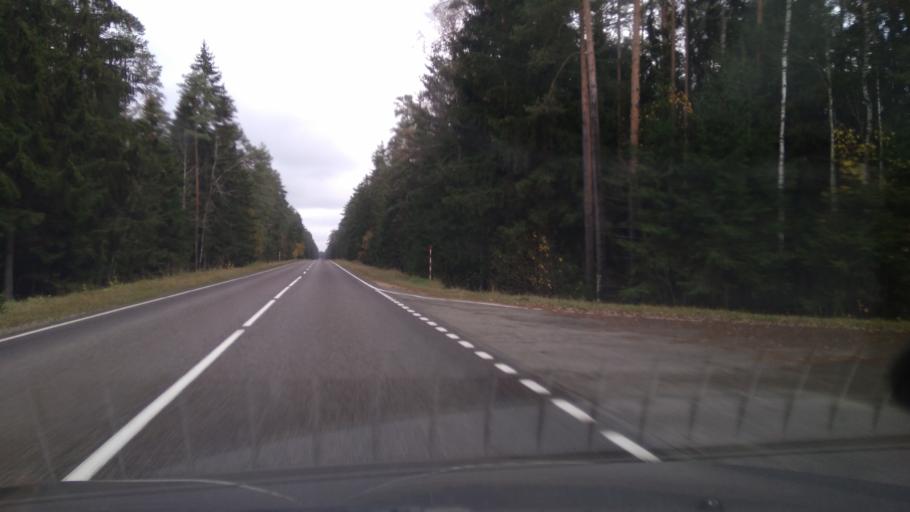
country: BY
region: Minsk
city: Urechcha
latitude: 53.2069
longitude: 27.8044
